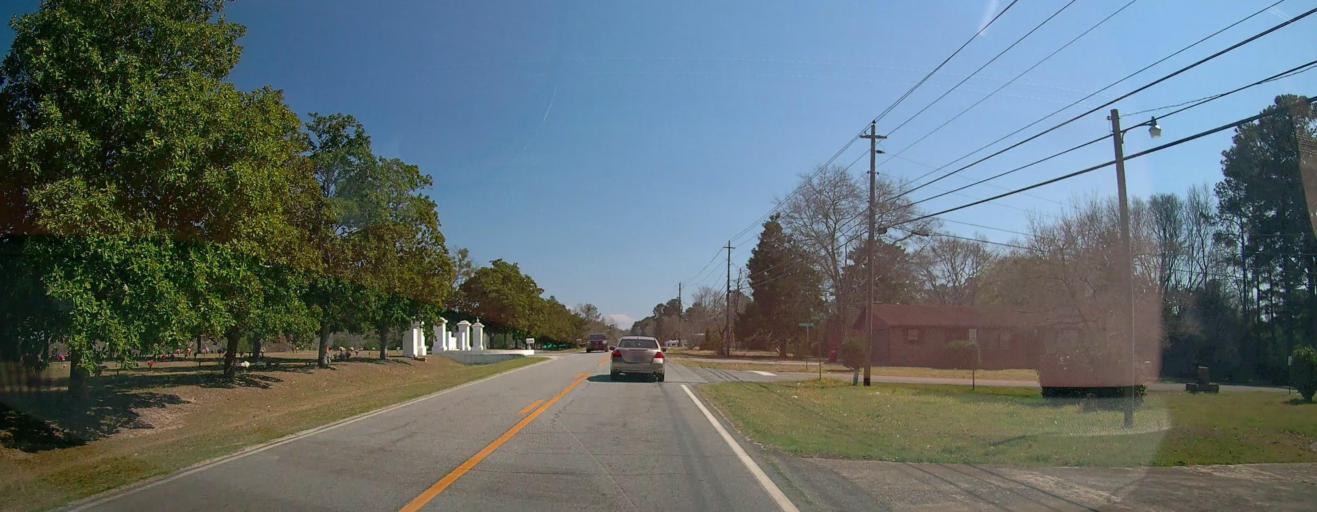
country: US
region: Georgia
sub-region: Bibb County
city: Macon
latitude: 32.8795
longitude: -83.5679
